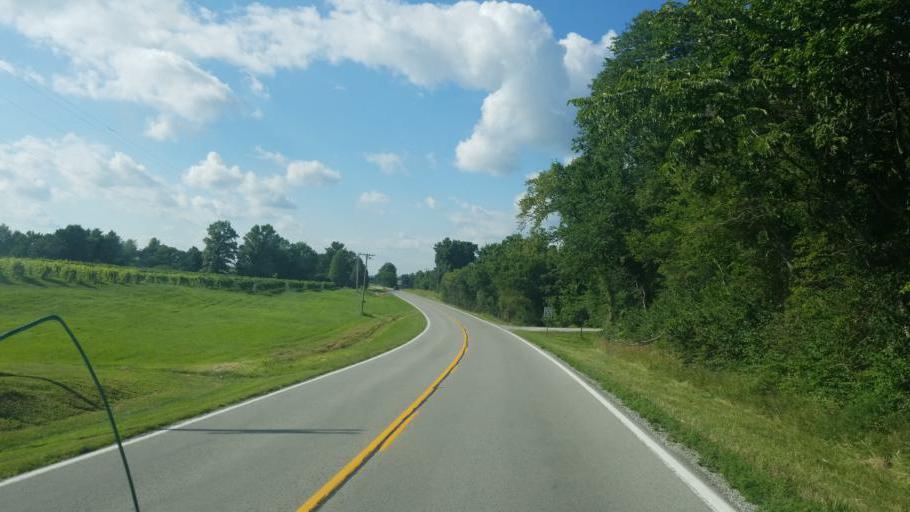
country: US
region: Illinois
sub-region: Union County
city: Cobden
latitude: 37.5799
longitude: -89.3205
